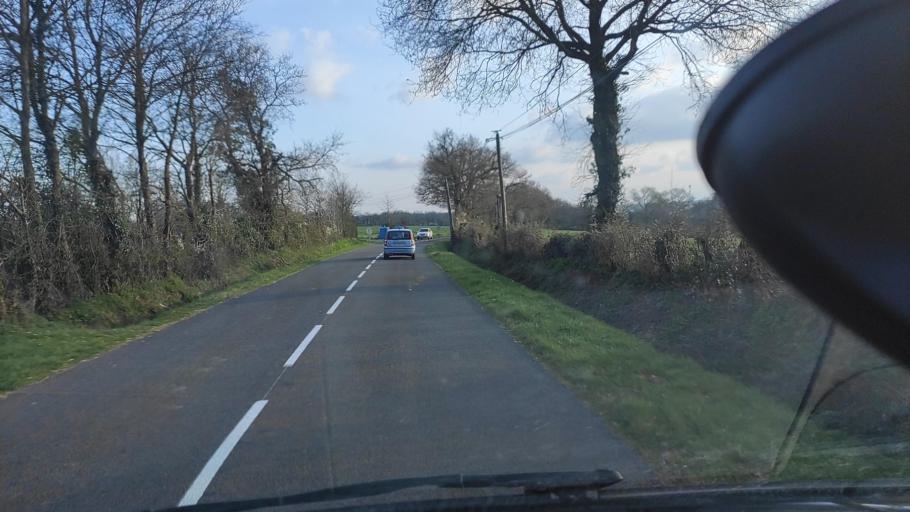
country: FR
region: Pays de la Loire
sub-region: Departement de la Vendee
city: La Chaize-le-Vicomte
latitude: 46.6350
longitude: -1.3028
